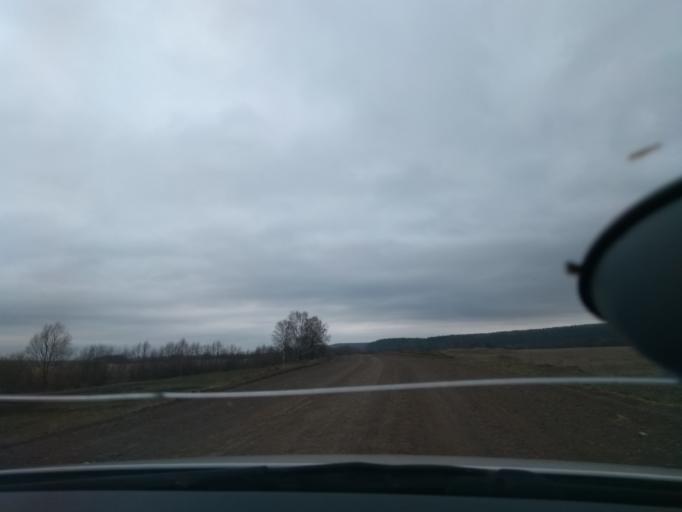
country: RU
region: Perm
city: Orda
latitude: 57.2289
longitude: 56.6042
